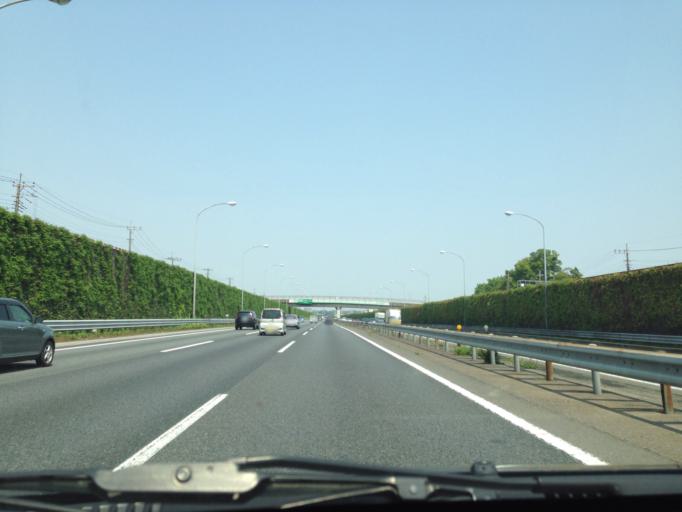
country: JP
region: Saitama
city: Iwatsuki
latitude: 35.9143
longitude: 139.7069
